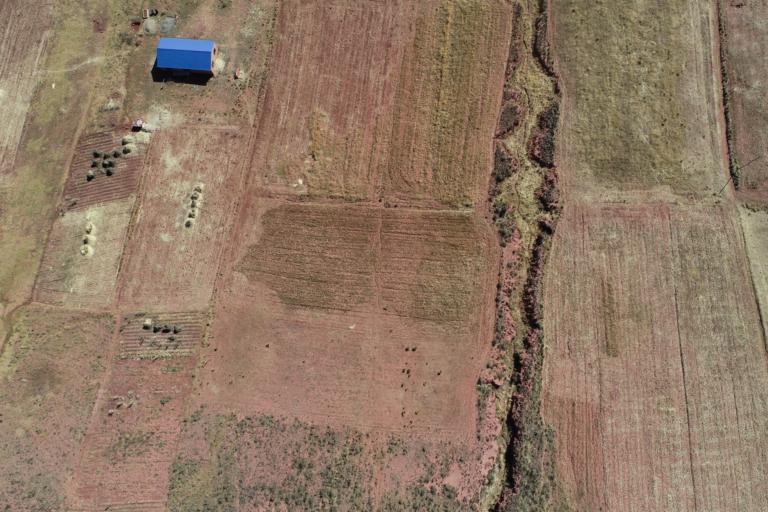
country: BO
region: La Paz
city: Tiahuanaco
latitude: -16.5952
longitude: -68.7567
